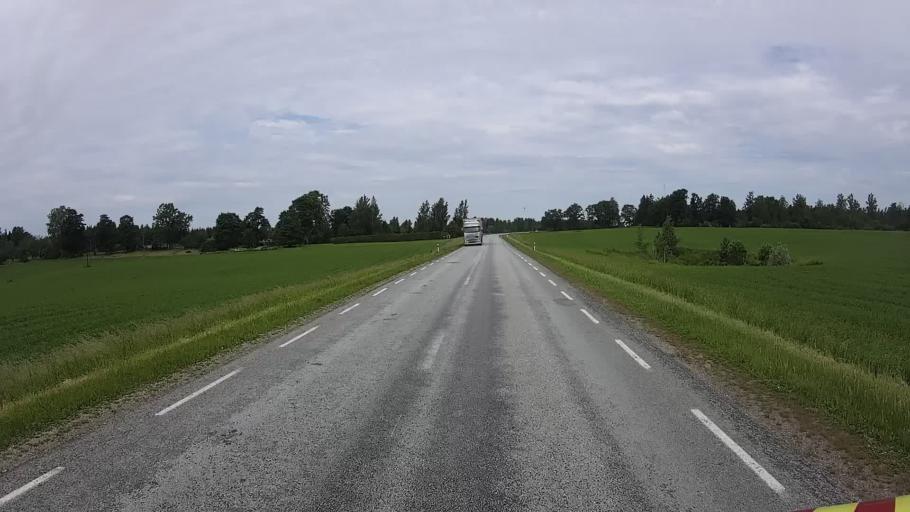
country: EE
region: Viljandimaa
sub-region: Karksi vald
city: Karksi-Nuia
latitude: 58.2268
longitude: 25.6085
